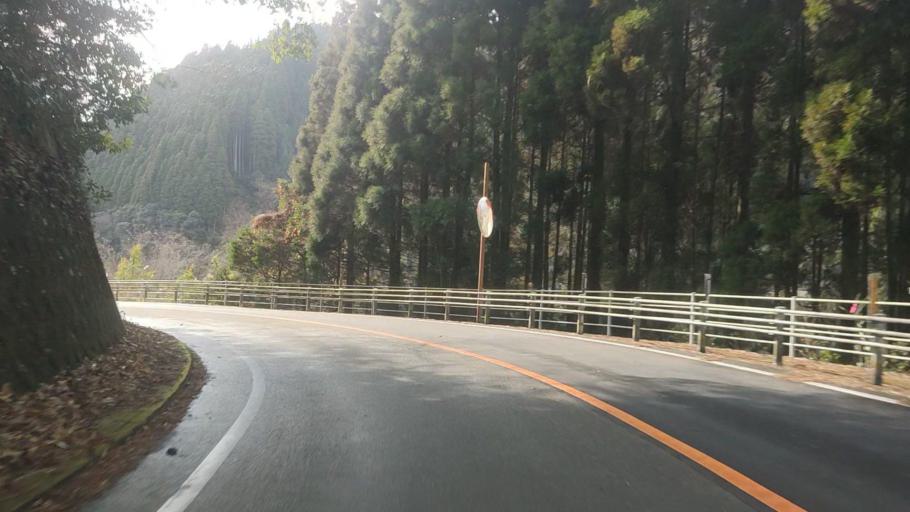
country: JP
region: Kumamoto
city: Hitoyoshi
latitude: 32.2918
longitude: 130.8421
